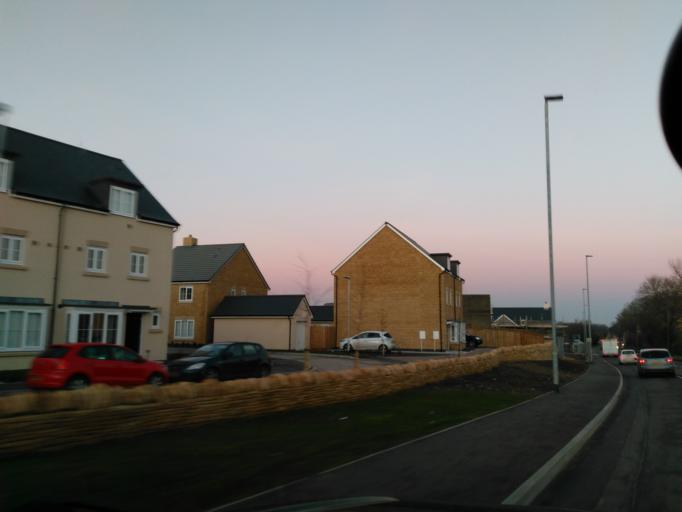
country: GB
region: England
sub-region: Wiltshire
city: Neston
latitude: 51.4332
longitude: -2.2070
